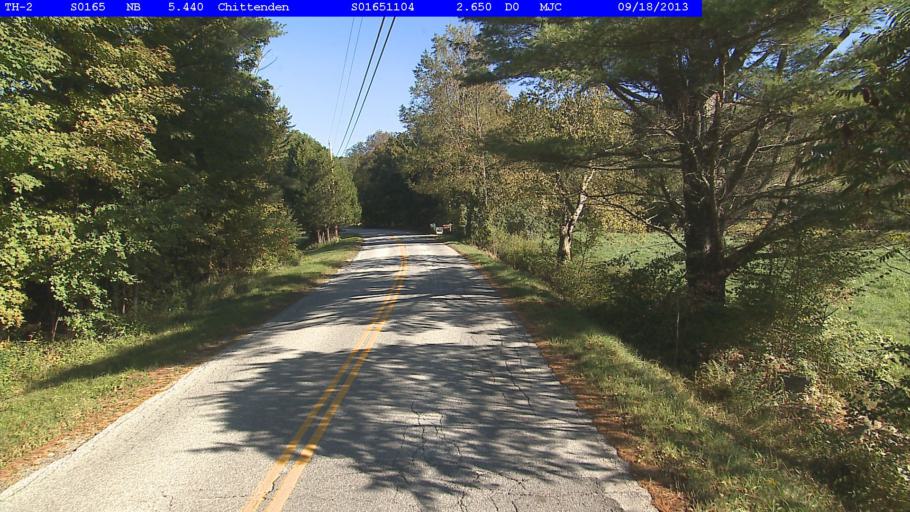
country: US
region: Vermont
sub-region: Rutland County
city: Rutland
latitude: 43.7138
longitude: -72.9612
